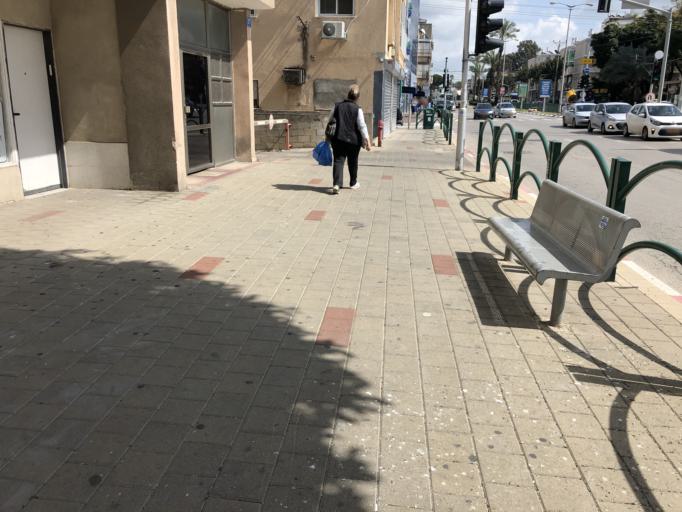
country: IL
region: Haifa
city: Hadera
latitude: 32.4403
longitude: 34.9181
